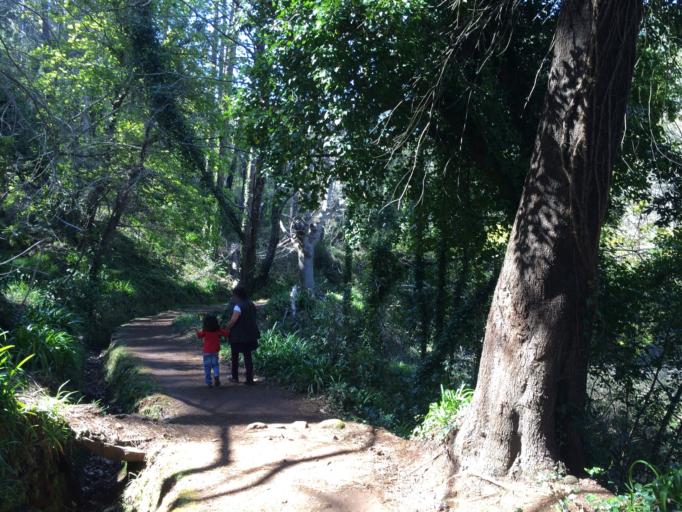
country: PT
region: Madeira
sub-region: Santa Cruz
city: Camacha
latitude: 32.6825
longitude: -16.8570
